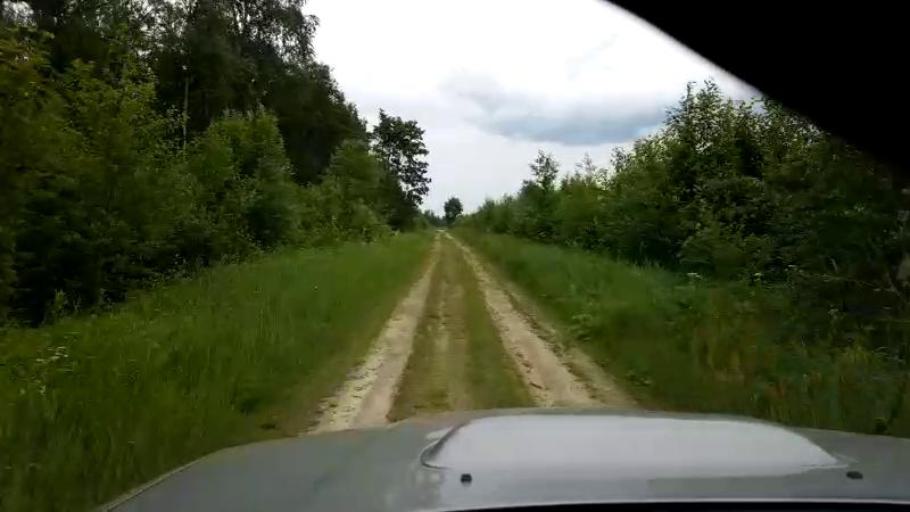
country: EE
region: Paernumaa
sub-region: Halinga vald
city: Parnu-Jaagupi
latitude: 58.5359
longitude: 24.6168
